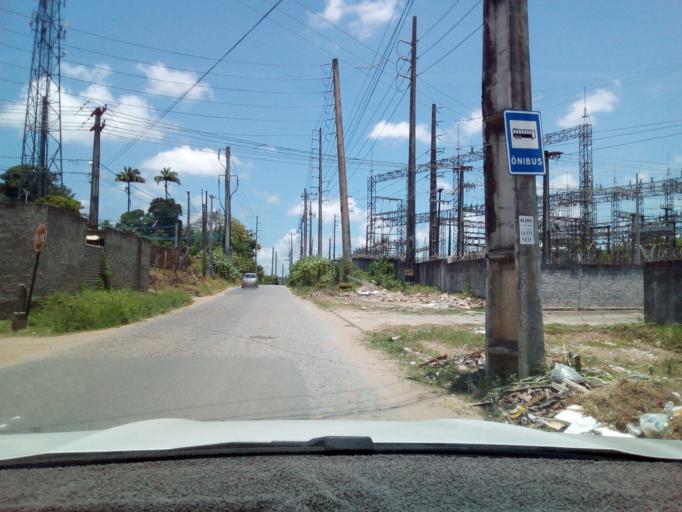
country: BR
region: Paraiba
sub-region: Bayeux
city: Bayeux
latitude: -7.1793
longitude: -34.8934
